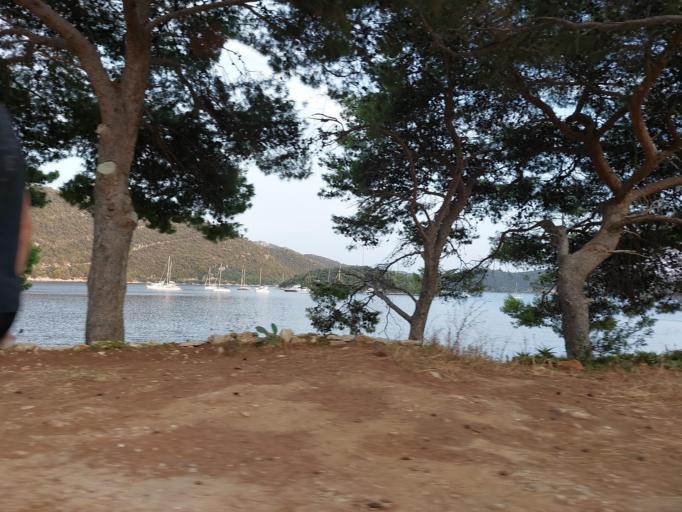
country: HR
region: Dubrovacko-Neretvanska
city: Smokvica
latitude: 42.7643
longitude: 16.8174
